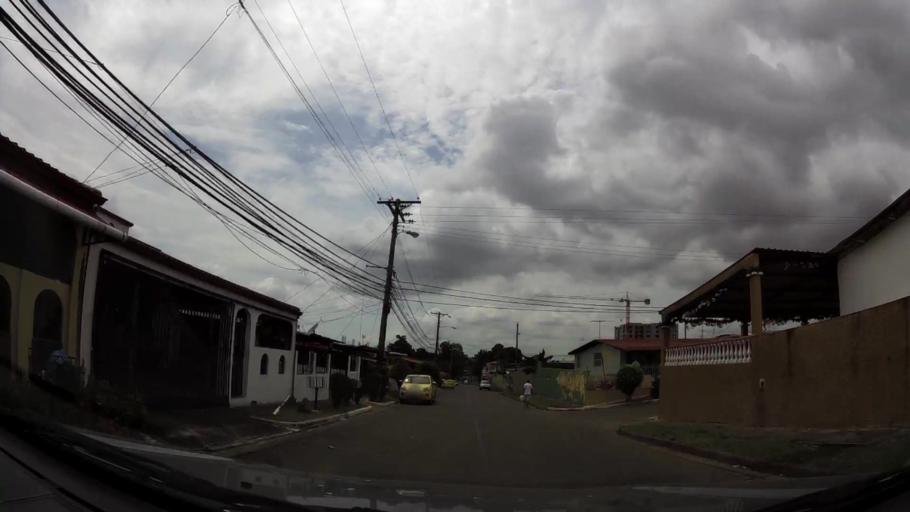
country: PA
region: Panama
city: San Miguelito
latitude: 9.0531
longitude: -79.4225
